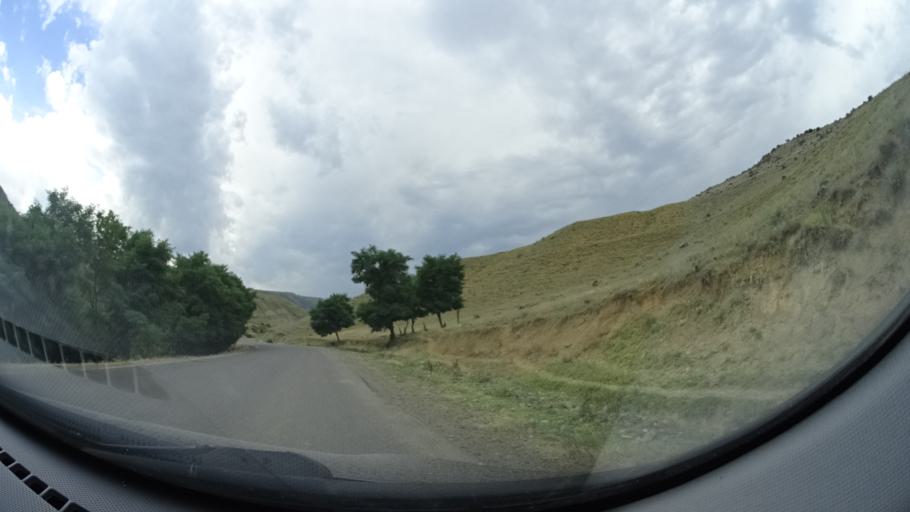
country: GE
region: Samtskhe-Javakheti
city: Aspindza
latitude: 41.5960
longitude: 43.2037
